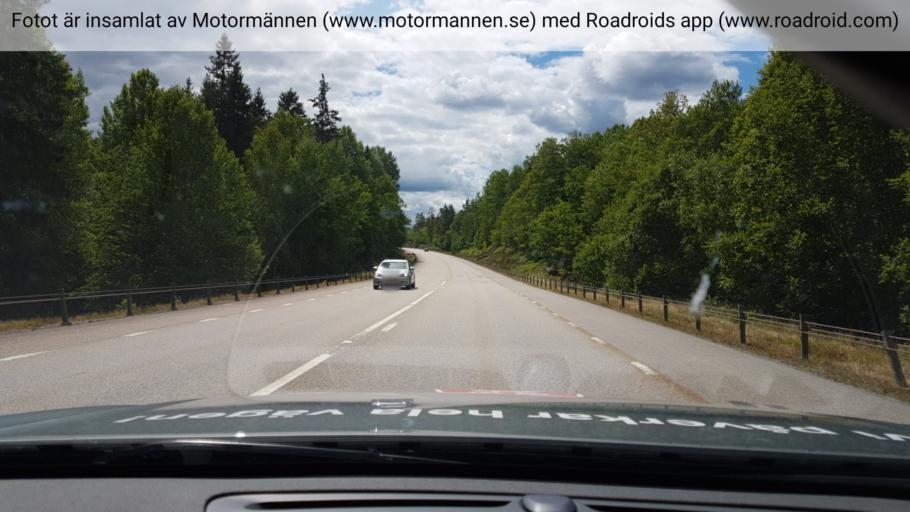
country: SE
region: Kalmar
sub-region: Vasterviks Kommun
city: Ankarsrum
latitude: 57.5617
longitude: 16.4767
